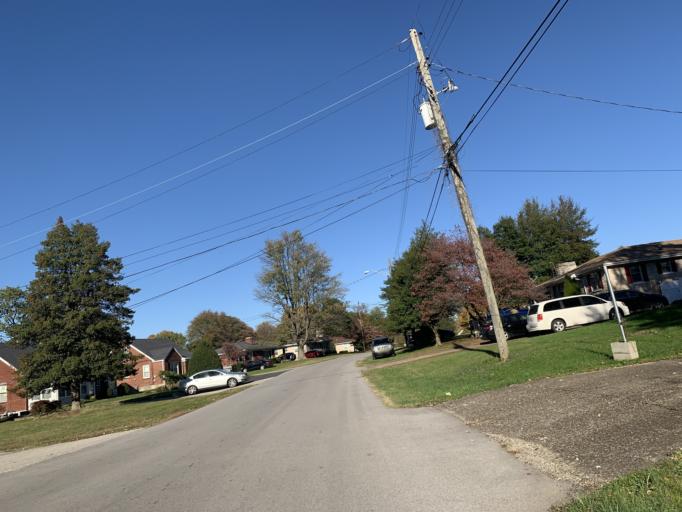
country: US
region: Kentucky
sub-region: Jefferson County
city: Saint Dennis
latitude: 38.1708
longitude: -85.8290
